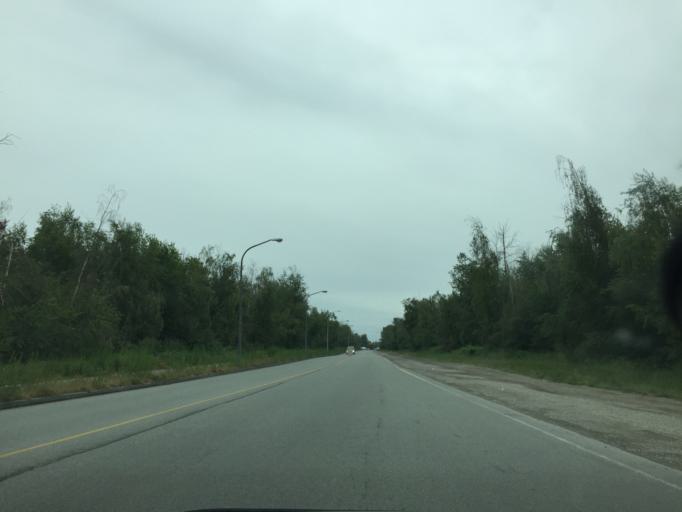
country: CA
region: British Columbia
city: Richmond
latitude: 49.1756
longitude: -123.1031
